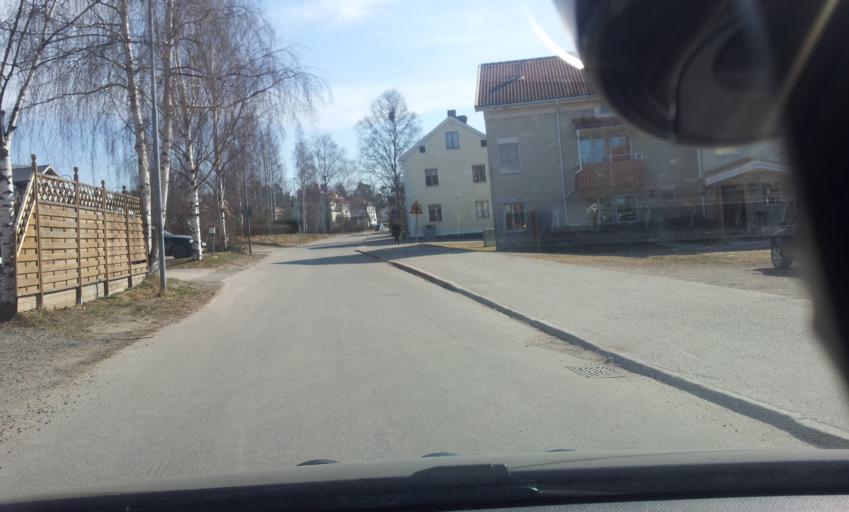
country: SE
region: Gaevleborg
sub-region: Ljusdals Kommun
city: Ljusdal
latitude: 61.8311
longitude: 16.0950
